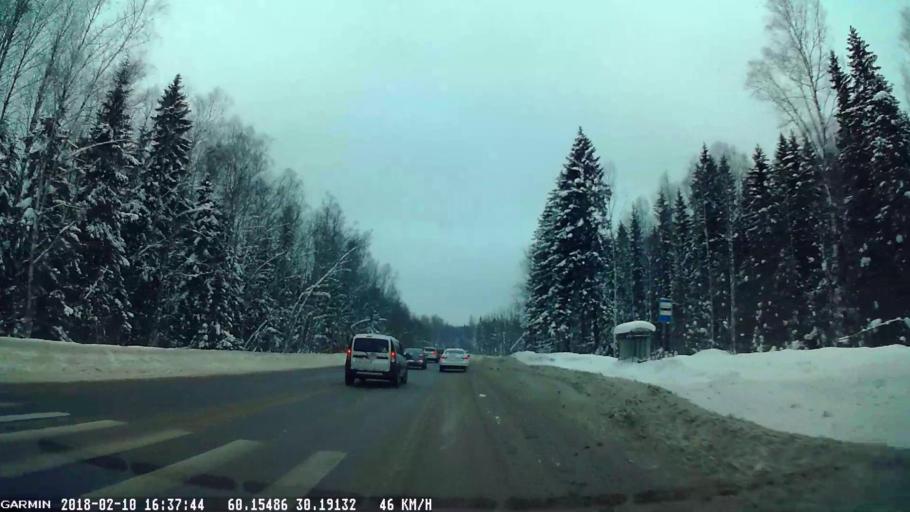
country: RU
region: Leningrad
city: Sertolovo
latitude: 60.1514
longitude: 30.1957
